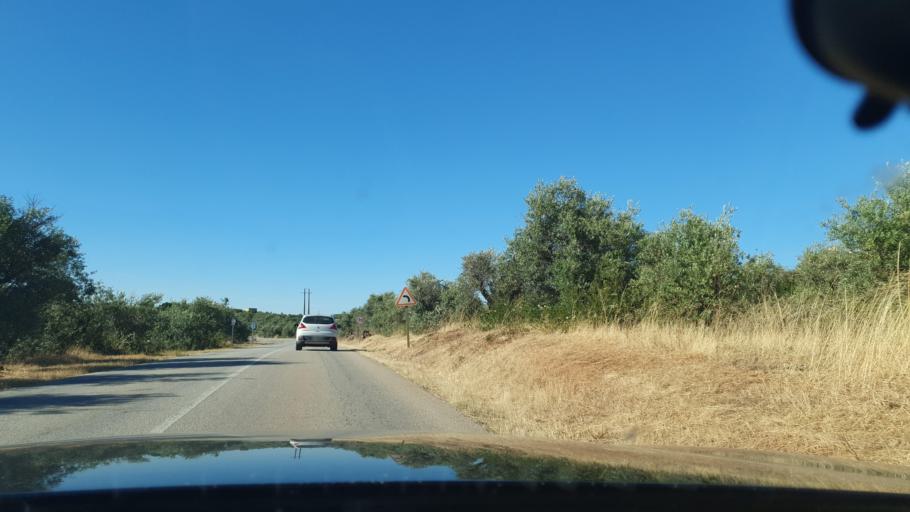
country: PT
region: Evora
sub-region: Vila Vicosa
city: Vila Vicosa
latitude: 38.7488
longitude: -7.4091
